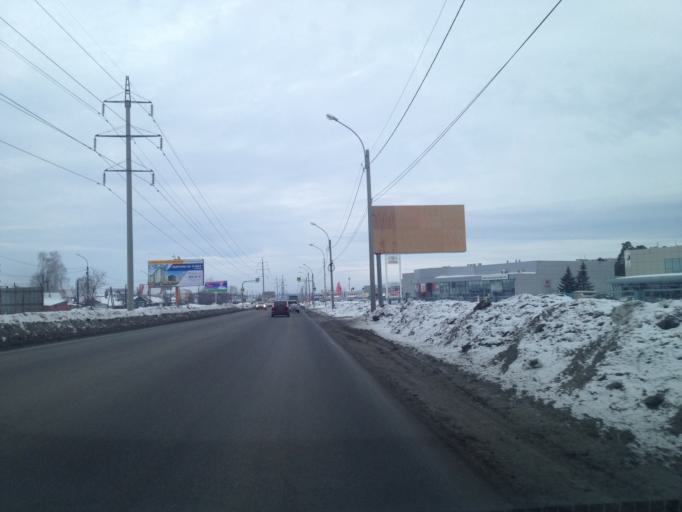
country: RU
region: Sverdlovsk
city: Sovkhoznyy
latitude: 56.7634
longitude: 60.5912
